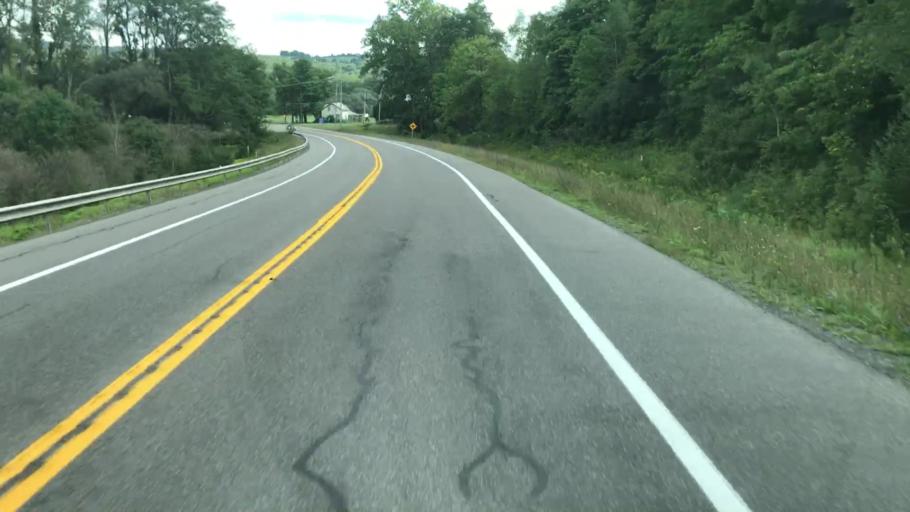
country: US
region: New York
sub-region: Onondaga County
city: Marcellus
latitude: 42.9511
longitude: -76.3554
